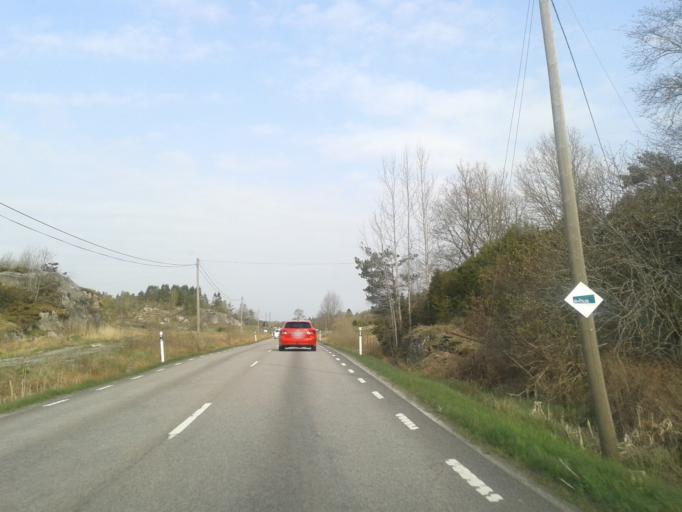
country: SE
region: Vaestra Goetaland
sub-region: Kungalvs Kommun
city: Kode
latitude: 57.8872
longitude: 11.8884
